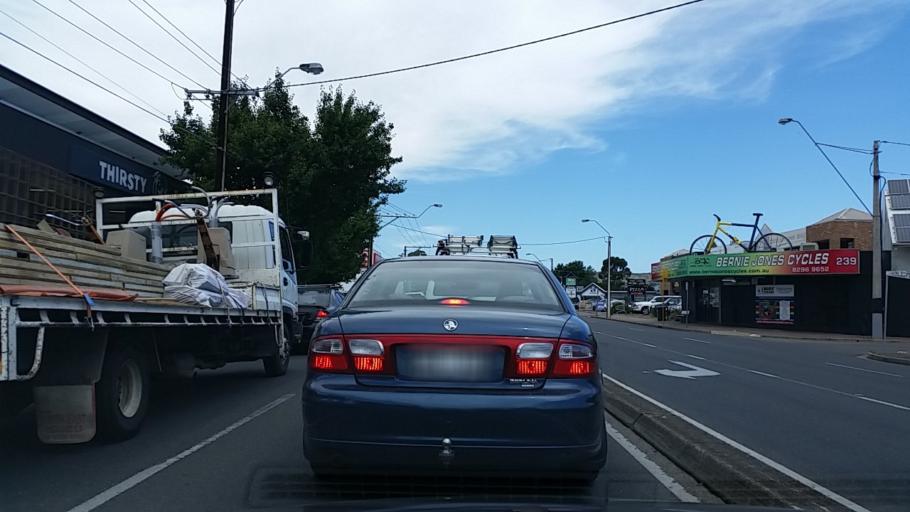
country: AU
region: South Australia
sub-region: Marion
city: Sturt
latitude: -35.0079
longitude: 138.5386
